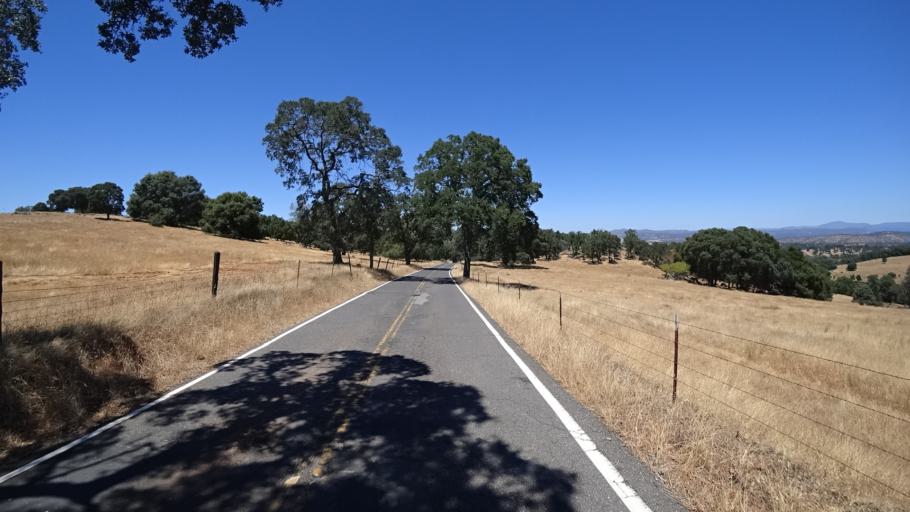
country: US
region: California
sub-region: Calaveras County
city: Copperopolis
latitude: 38.0858
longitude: -120.6622
